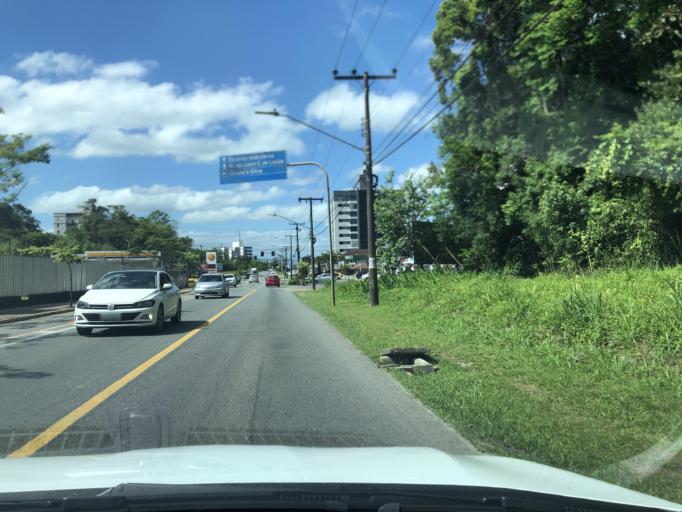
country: BR
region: Santa Catarina
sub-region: Joinville
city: Joinville
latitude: -26.2765
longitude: -48.8635
